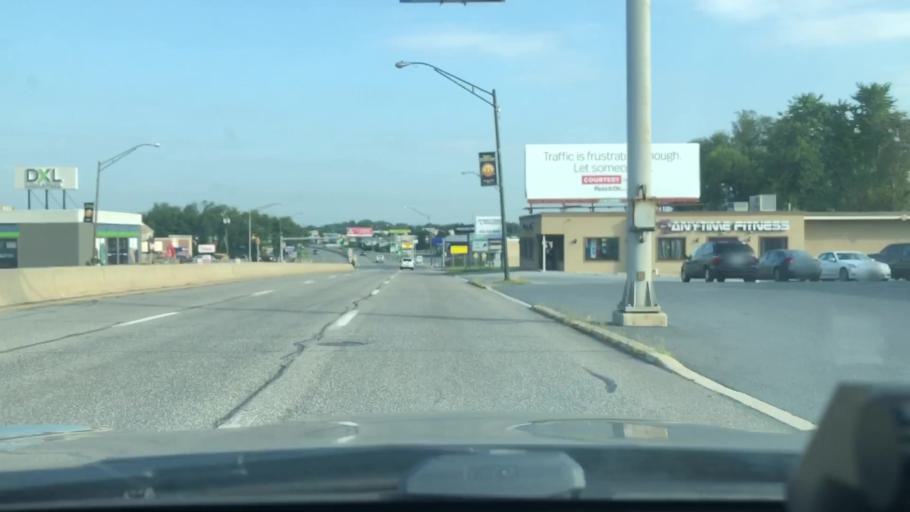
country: US
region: Pennsylvania
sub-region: Lehigh County
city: Fullerton
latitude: 40.6404
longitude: -75.4896
